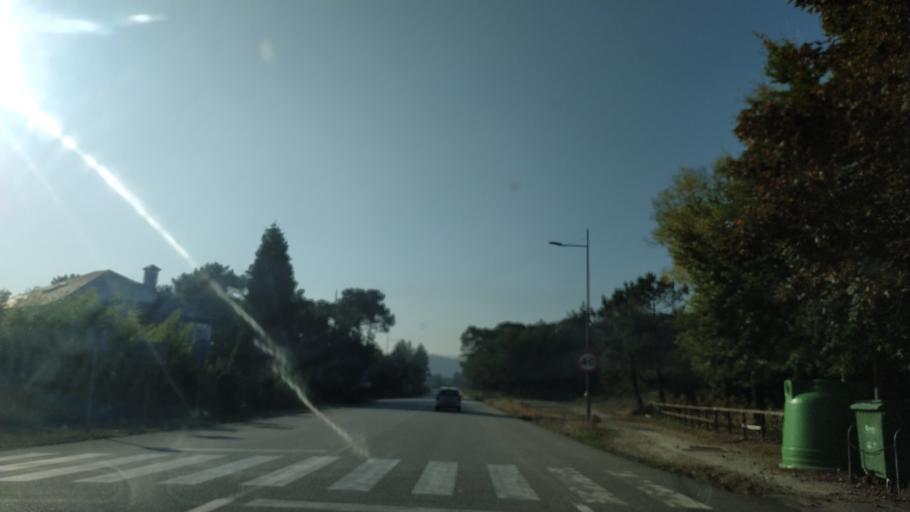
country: ES
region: Galicia
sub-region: Provincia da Coruna
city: Carballo
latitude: 43.2320
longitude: -8.6789
